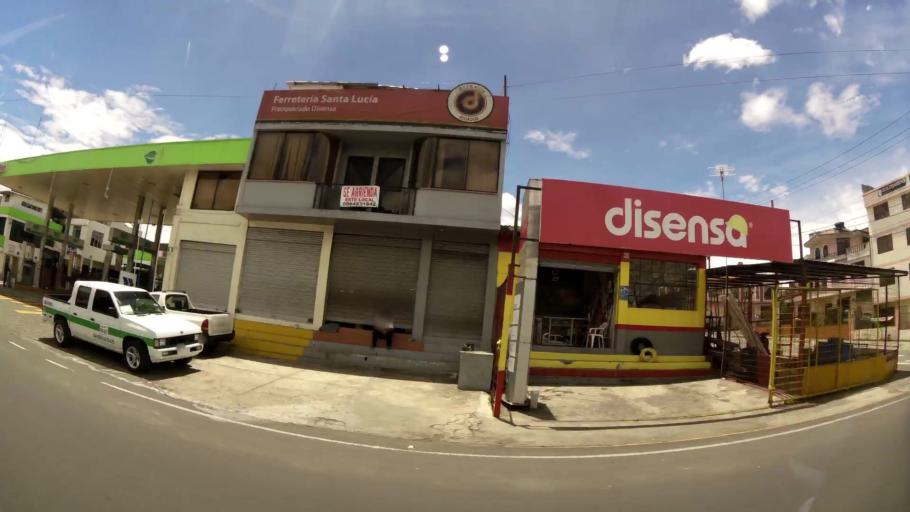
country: EC
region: Tungurahua
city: Pelileo
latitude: -1.3262
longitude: -78.5430
